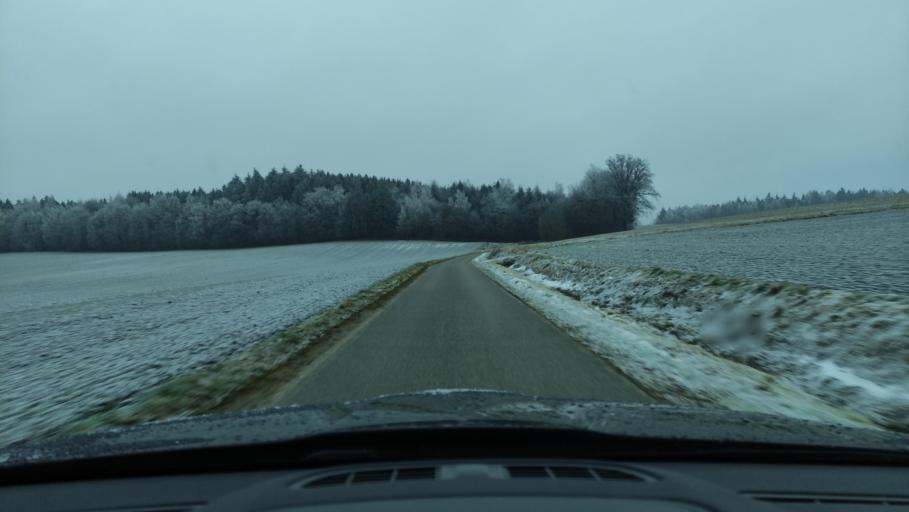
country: DE
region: Bavaria
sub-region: Swabia
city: Deisenhausen
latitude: 48.2642
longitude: 10.3367
